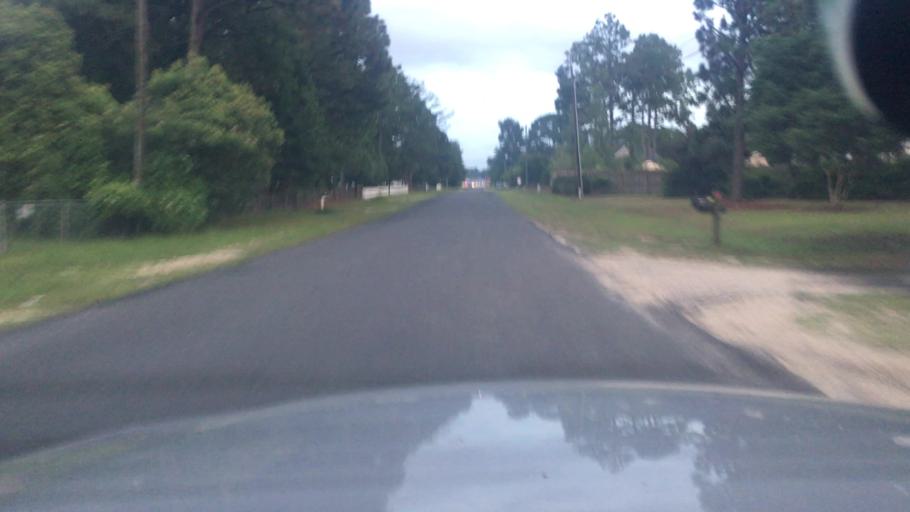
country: US
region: North Carolina
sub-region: Cumberland County
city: Hope Mills
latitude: 34.9844
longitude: -78.9121
